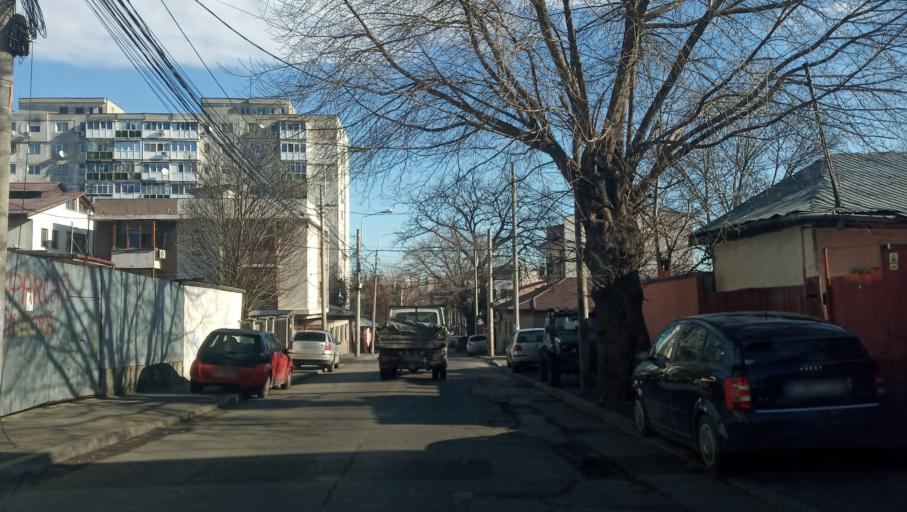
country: RO
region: Ilfov
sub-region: Comuna Fundeni-Dobroesti
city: Fundeni
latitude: 44.4621
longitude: 26.1363
